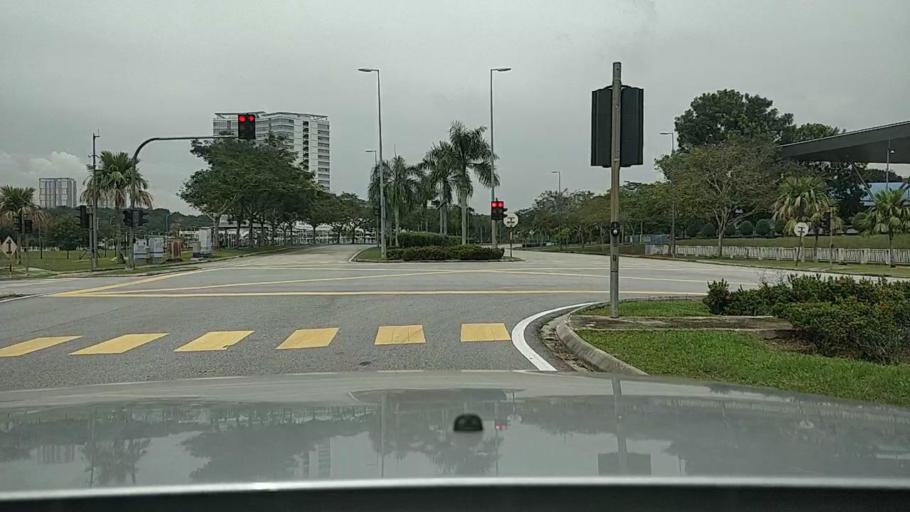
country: MY
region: Putrajaya
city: Putrajaya
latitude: 2.9061
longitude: 101.6519
